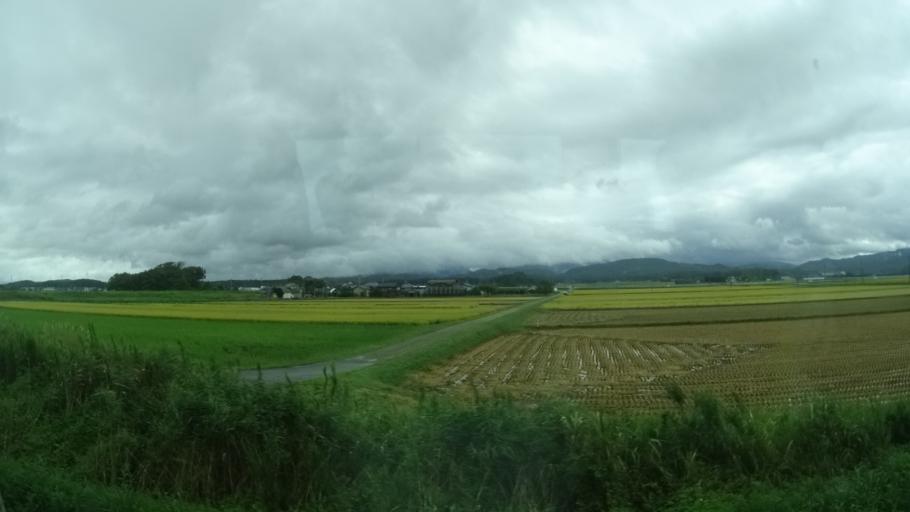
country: JP
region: Niigata
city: Murakami
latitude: 38.1908
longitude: 139.4599
